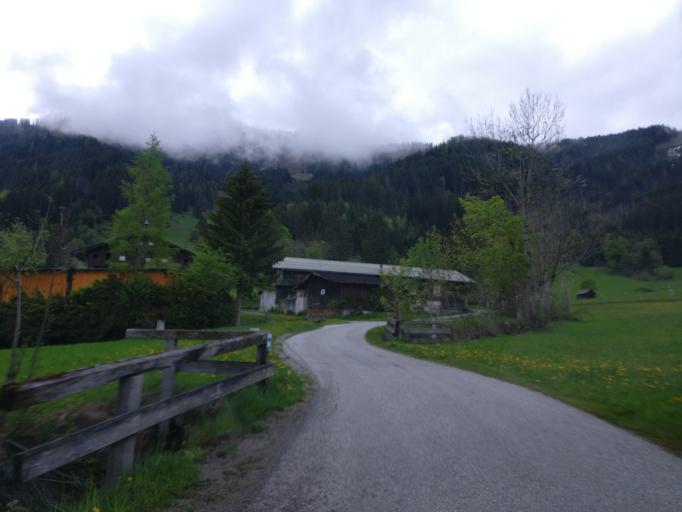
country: AT
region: Salzburg
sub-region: Politischer Bezirk Sankt Johann im Pongau
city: Werfenweng
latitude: 47.4574
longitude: 13.2761
